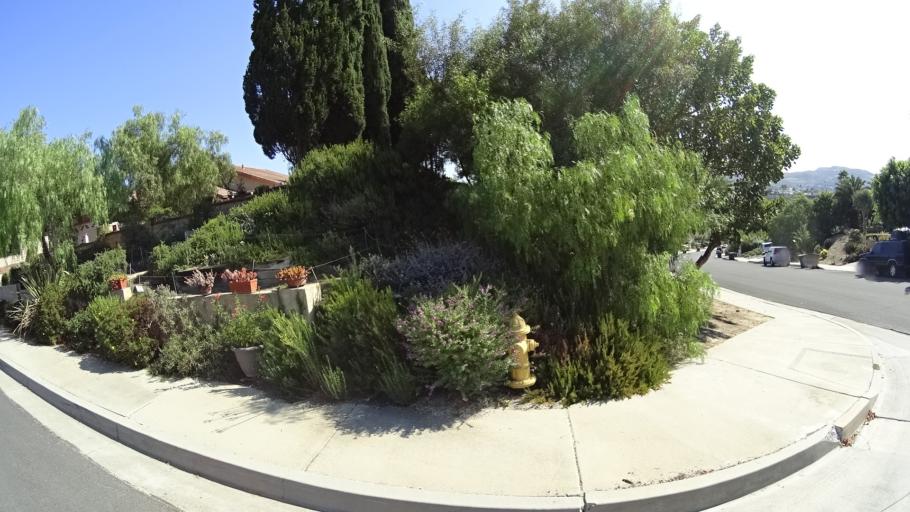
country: US
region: California
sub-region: Orange County
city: San Juan Capistrano
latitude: 33.4749
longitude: -117.6391
